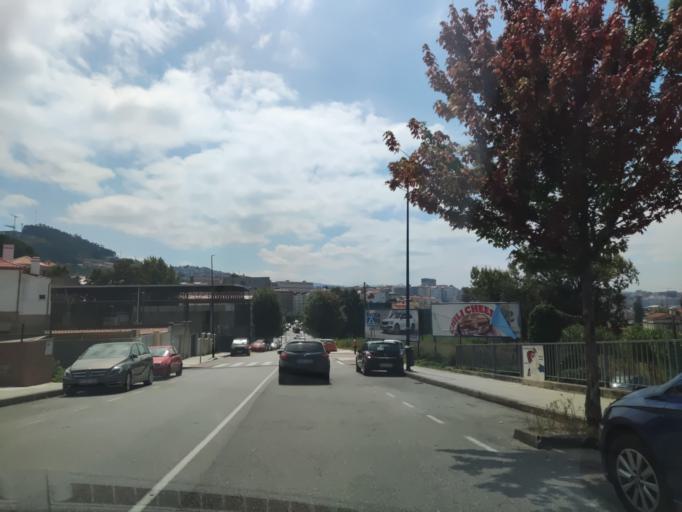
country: ES
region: Galicia
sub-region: Provincia de Pontevedra
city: Vigo
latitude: 42.2523
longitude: -8.6988
